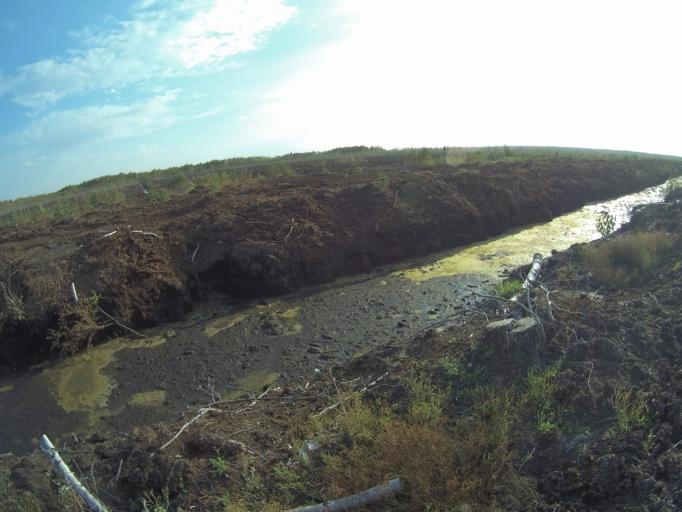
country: RU
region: Vladimir
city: Urshel'skiy
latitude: 55.7999
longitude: 40.1142
